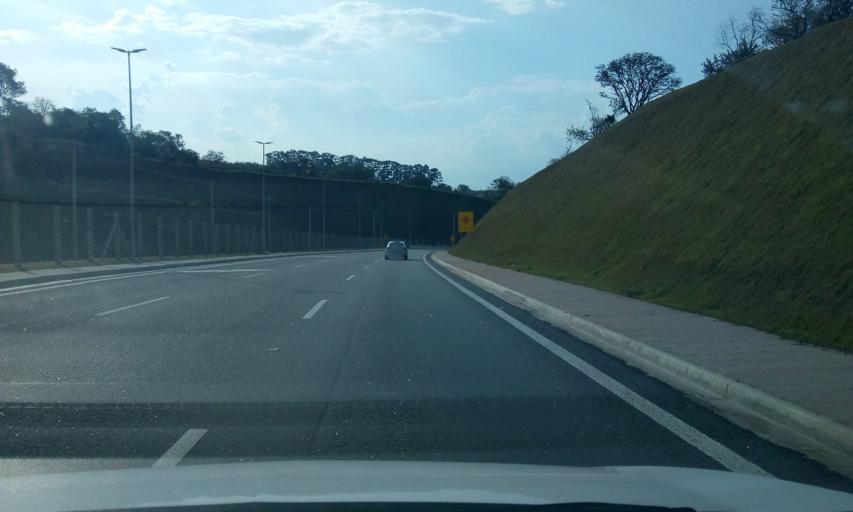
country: BR
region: Sao Paulo
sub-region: Jundiai
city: Jundiai
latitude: -23.2085
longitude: -46.8985
